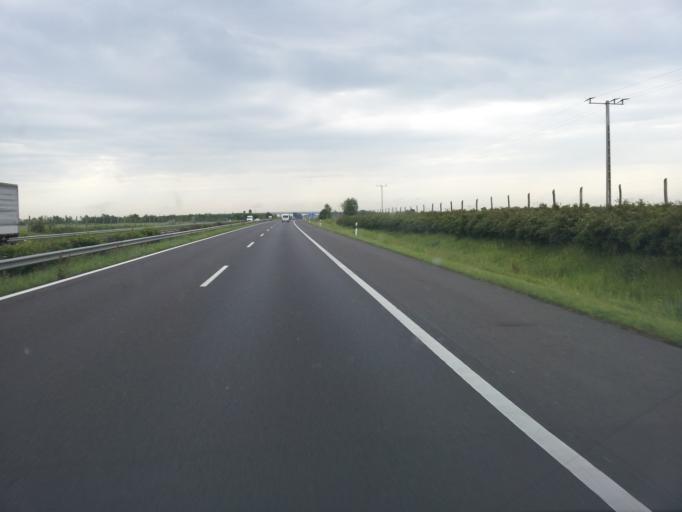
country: HU
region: Heves
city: Karacsond
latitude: 47.7063
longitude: 20.0913
